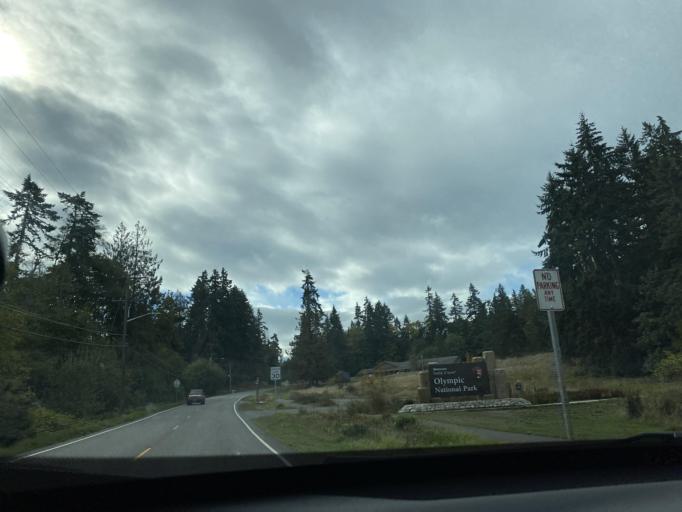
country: US
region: Washington
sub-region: Clallam County
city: Port Angeles
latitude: 48.1015
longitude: -123.4255
